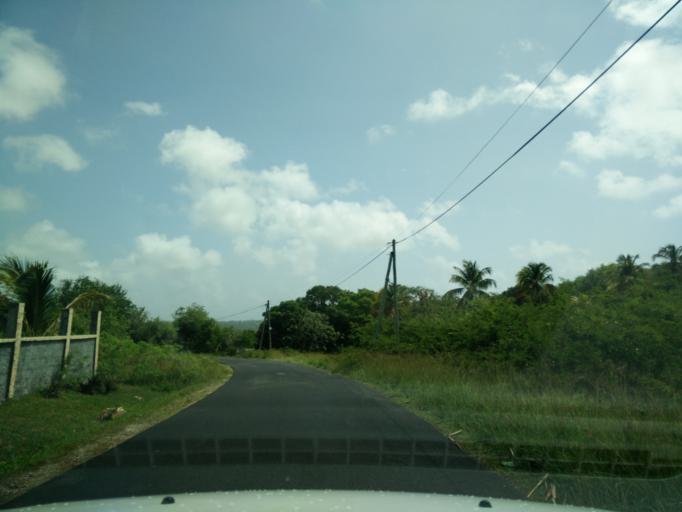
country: GP
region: Guadeloupe
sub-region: Guadeloupe
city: Grand-Bourg
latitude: 15.9099
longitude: -61.2761
